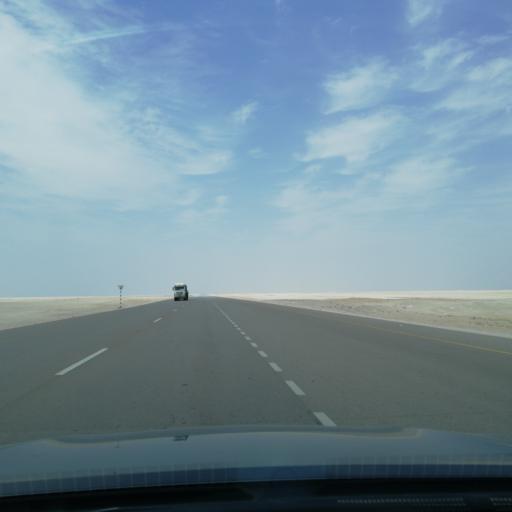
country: OM
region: Al Wusta
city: Hayma'
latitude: 20.1871
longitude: 56.5351
